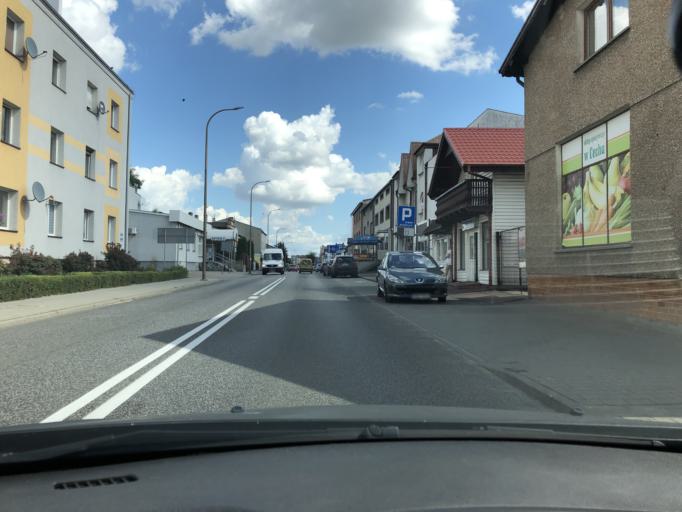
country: PL
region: Lodz Voivodeship
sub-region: Powiat wieruszowski
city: Wieruszow
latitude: 51.2946
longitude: 18.1571
